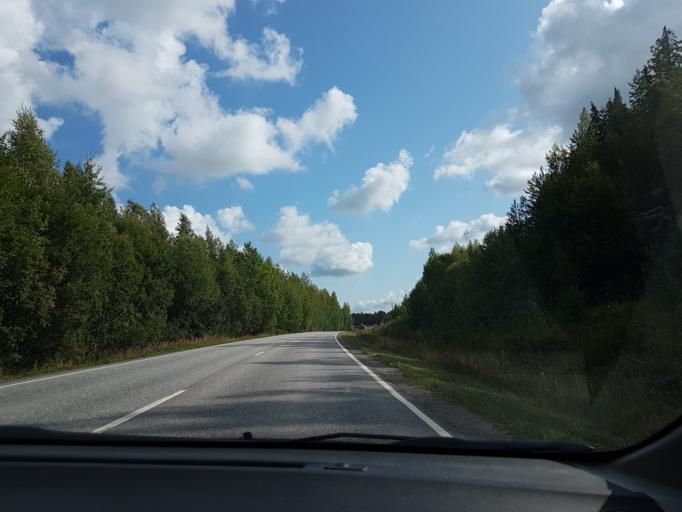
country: FI
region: Uusimaa
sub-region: Helsinki
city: Pornainen
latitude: 60.4717
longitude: 25.3005
